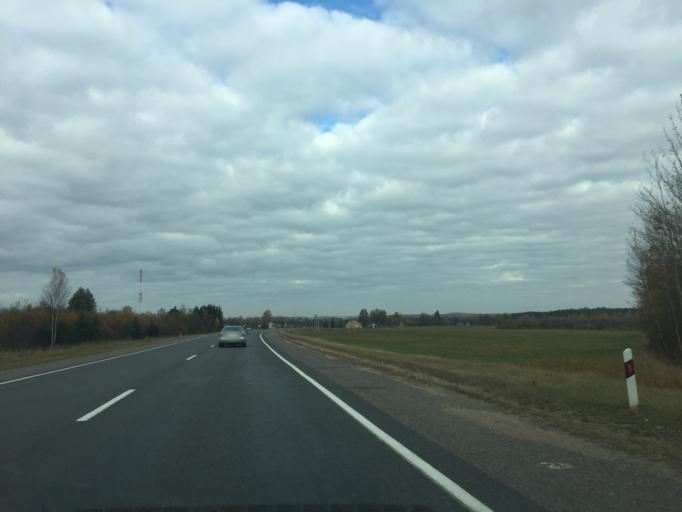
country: BY
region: Grodnenskaya
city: Kreva
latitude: 54.2052
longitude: 26.3600
